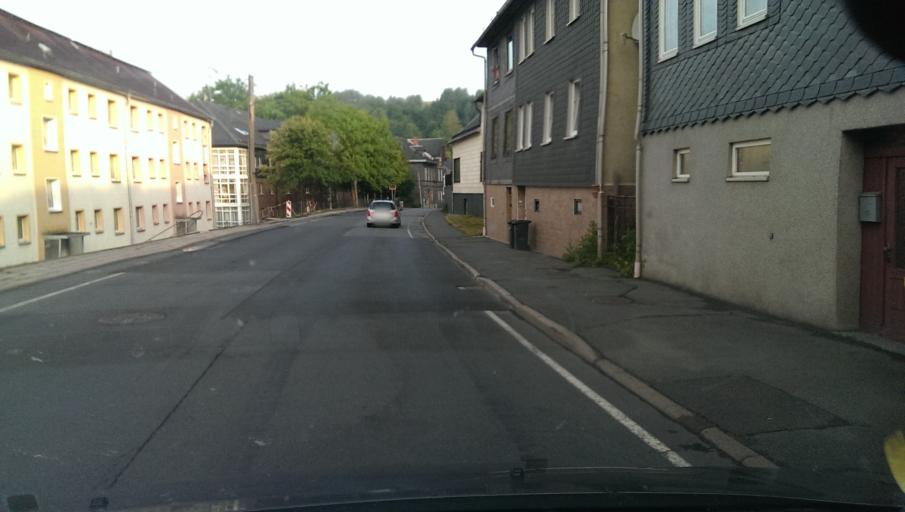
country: DE
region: Thuringia
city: Lichte
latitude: 50.5255
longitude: 11.1957
